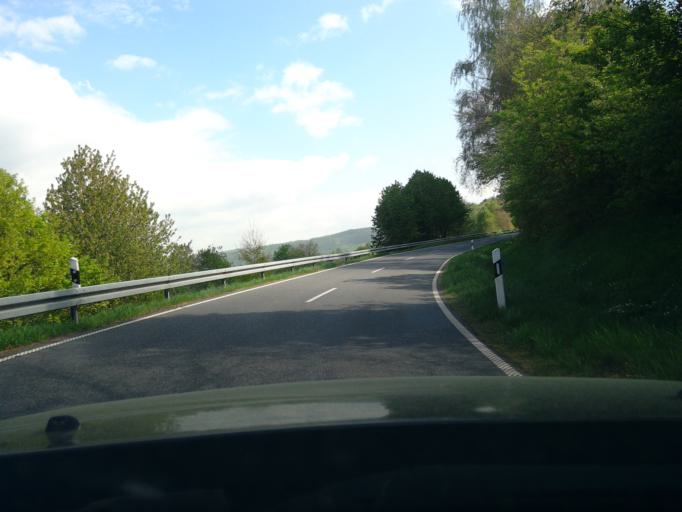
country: DE
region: Bavaria
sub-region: Regierungsbezirk Unterfranken
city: Kleinkahl
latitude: 50.1673
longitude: 9.2607
